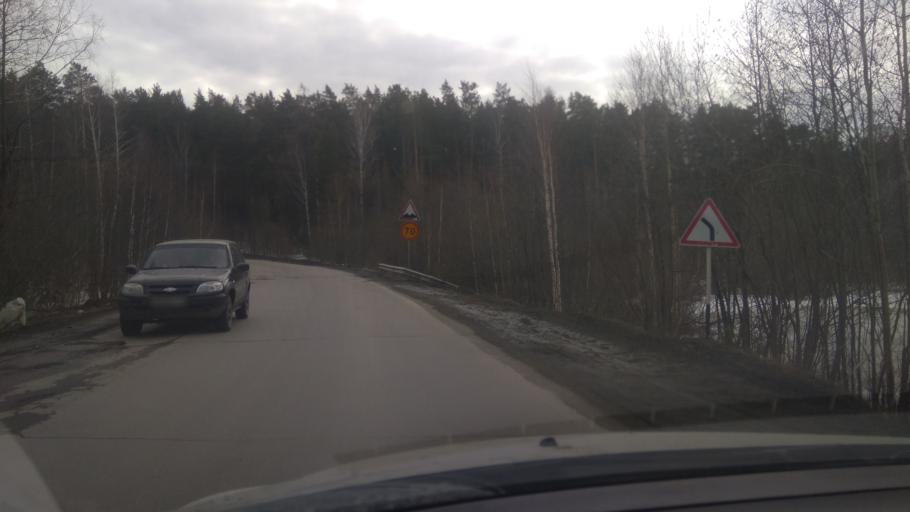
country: RU
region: Sverdlovsk
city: Severka
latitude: 56.8359
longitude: 60.3822
